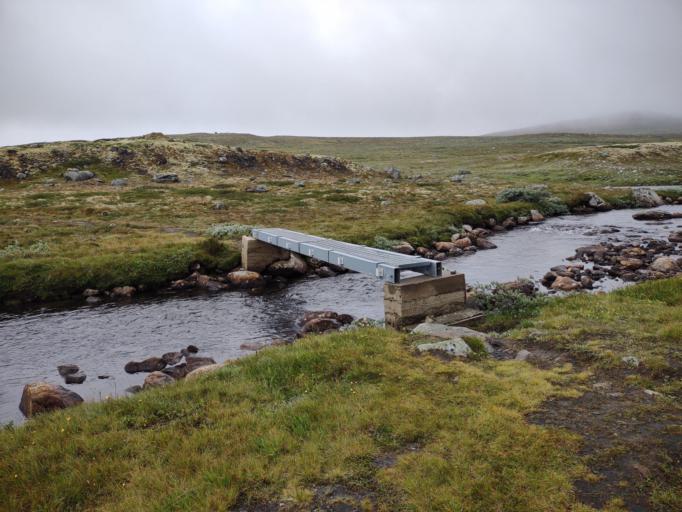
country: NO
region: Buskerud
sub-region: Hol
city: Geilo
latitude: 60.3963
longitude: 7.6555
